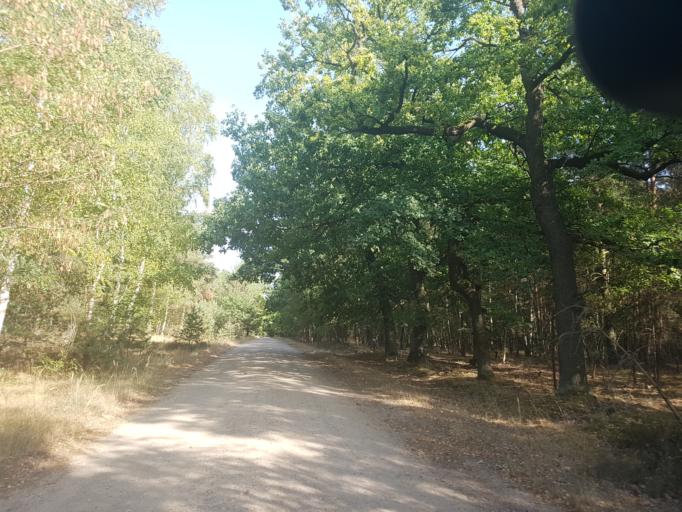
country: DE
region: Saxony-Anhalt
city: Jessen
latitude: 51.8704
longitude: 12.9994
